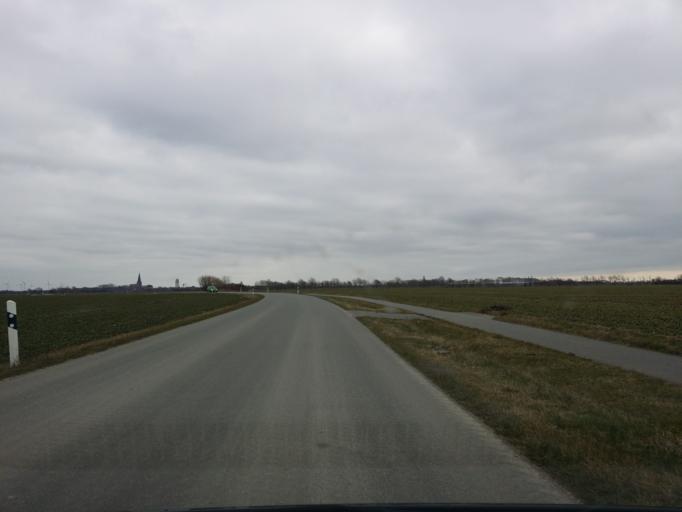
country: DE
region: Schleswig-Holstein
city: Grossenbrode
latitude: 54.4867
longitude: 11.0373
